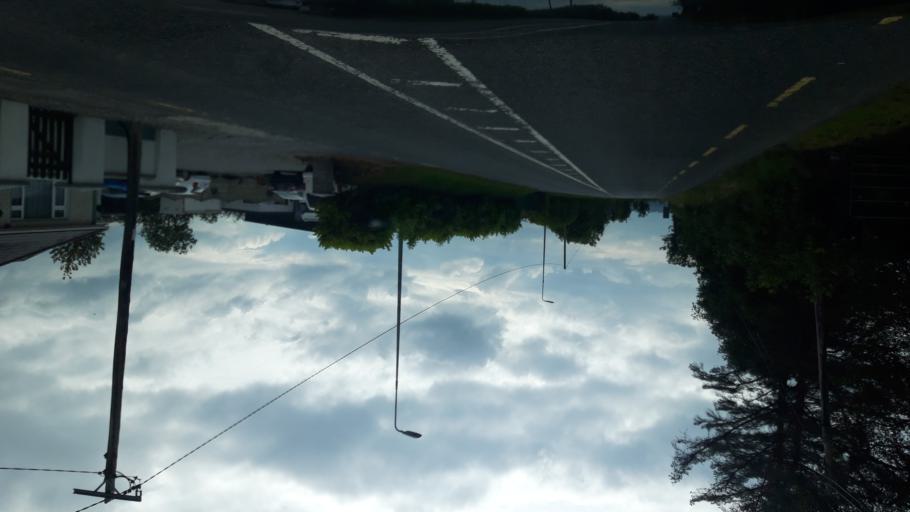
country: IE
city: Ballylinan
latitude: 52.8614
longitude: -7.1107
